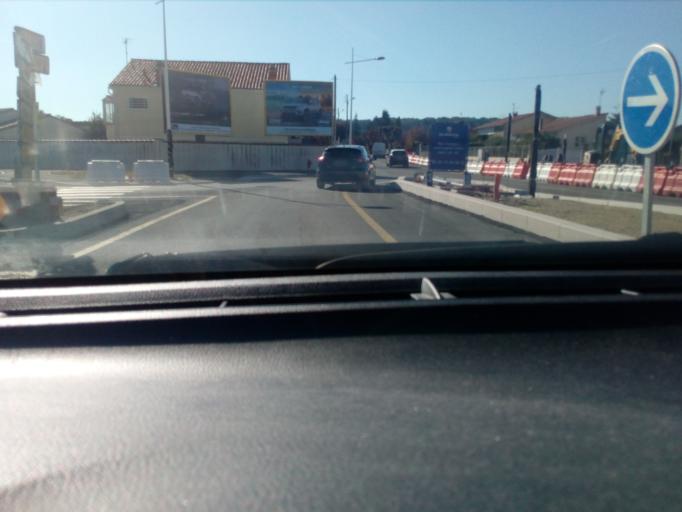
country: FR
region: Poitou-Charentes
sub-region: Departement de la Charente
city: Angouleme
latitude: 45.6459
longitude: 0.1330
